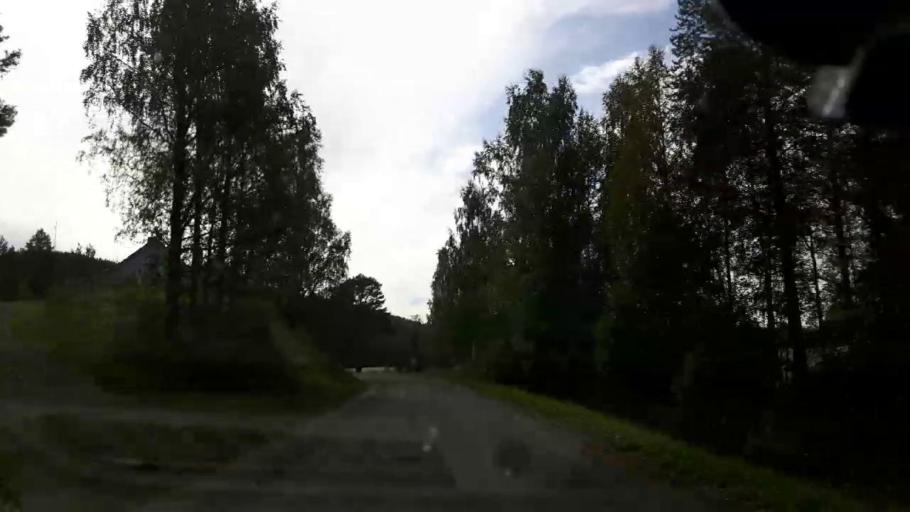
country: SE
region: Jaemtland
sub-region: Ragunda Kommun
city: Hammarstrand
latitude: 63.1431
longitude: 16.2036
